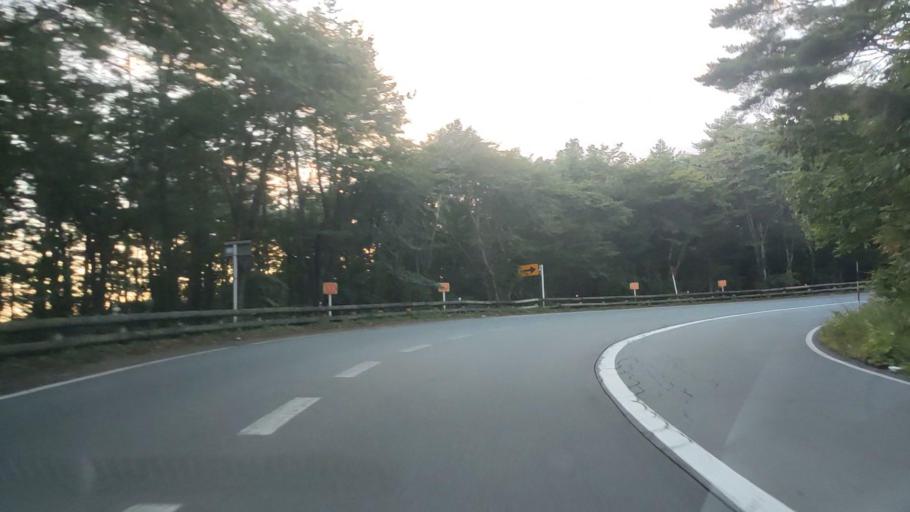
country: JP
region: Nagano
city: Komoro
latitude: 36.3872
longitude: 138.5863
